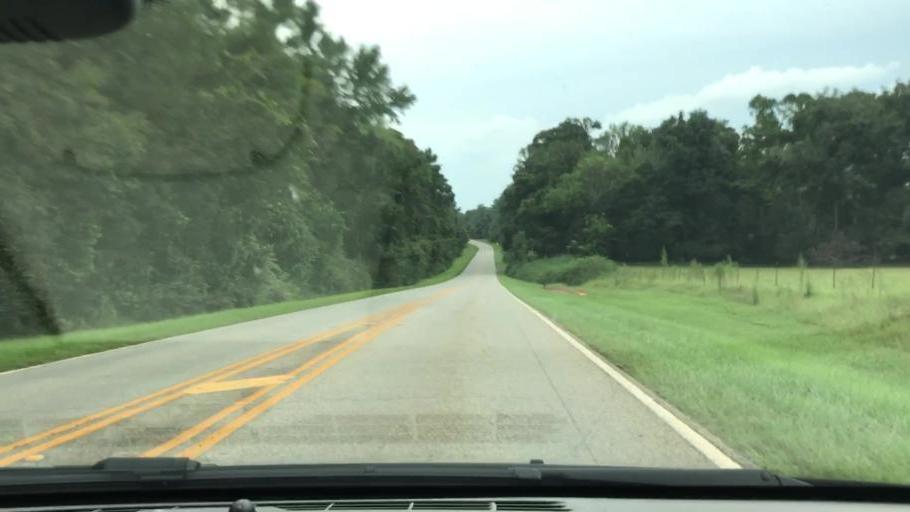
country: US
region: Georgia
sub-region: Early County
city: Blakely
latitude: 31.4072
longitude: -84.9285
